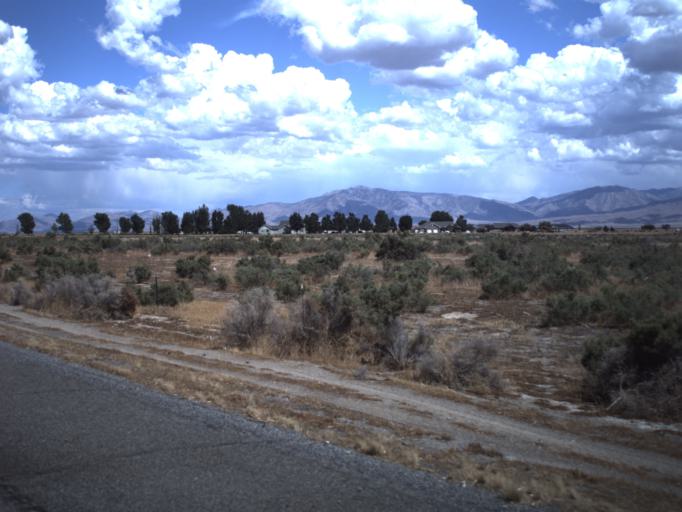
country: US
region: Utah
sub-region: Millard County
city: Delta
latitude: 39.3785
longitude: -112.5289
